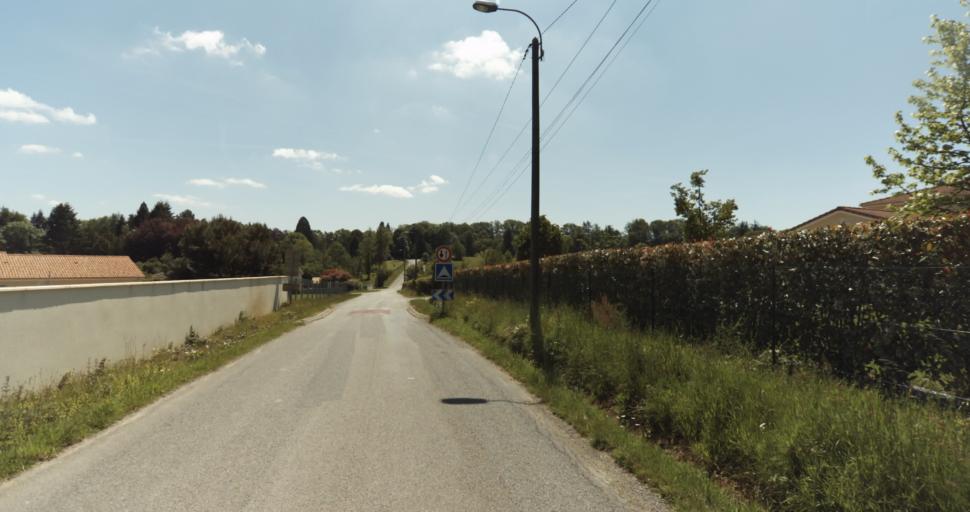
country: FR
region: Limousin
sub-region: Departement de la Haute-Vienne
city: Condat-sur-Vienne
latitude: 45.7910
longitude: 1.2944
